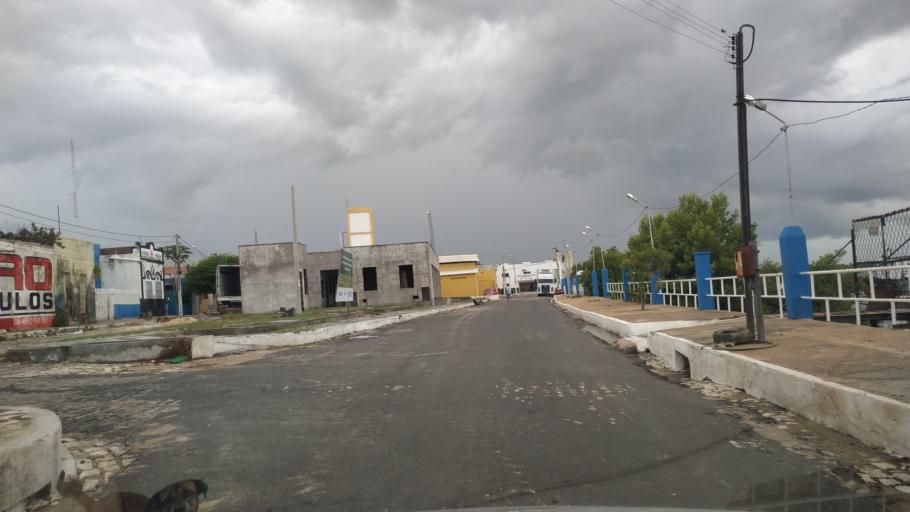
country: BR
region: Rio Grande do Norte
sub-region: Areia Branca
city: Areia Branca
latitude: -4.9569
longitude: -37.1371
